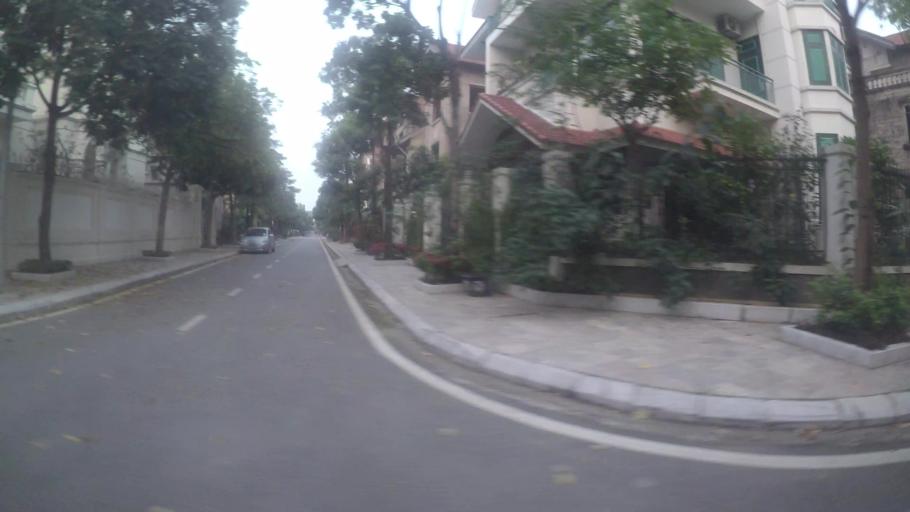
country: VN
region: Ha Noi
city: Cau Dien
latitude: 21.0000
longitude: 105.7304
